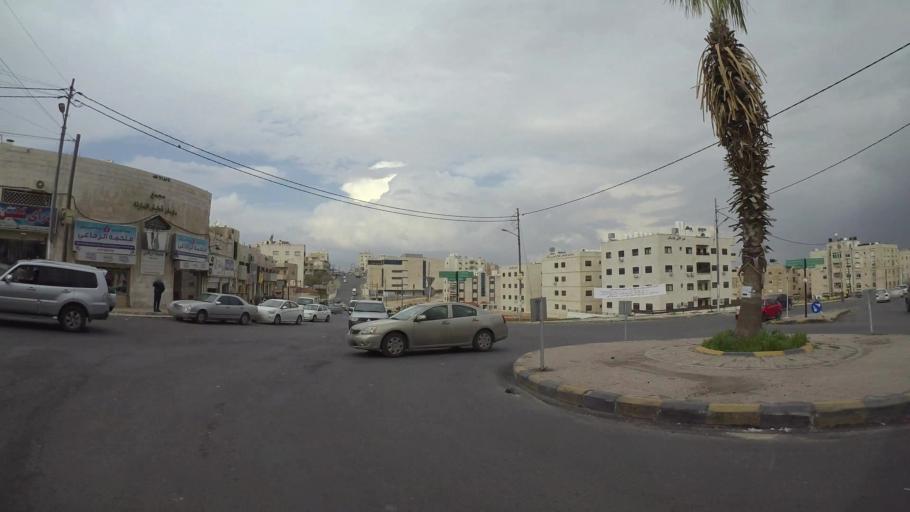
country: JO
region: Amman
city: Amman
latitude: 32.0004
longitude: 35.9477
